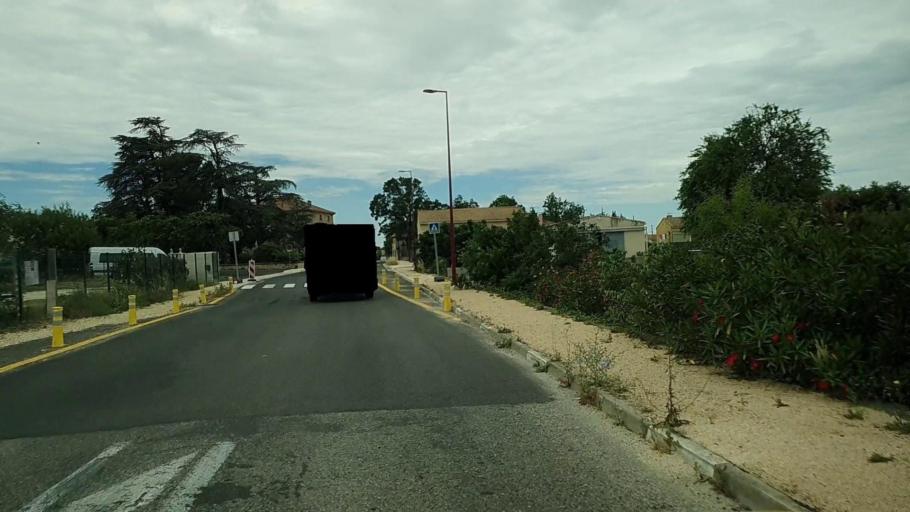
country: FR
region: Languedoc-Roussillon
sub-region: Departement du Gard
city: Connaux
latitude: 44.0388
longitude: 4.5817
